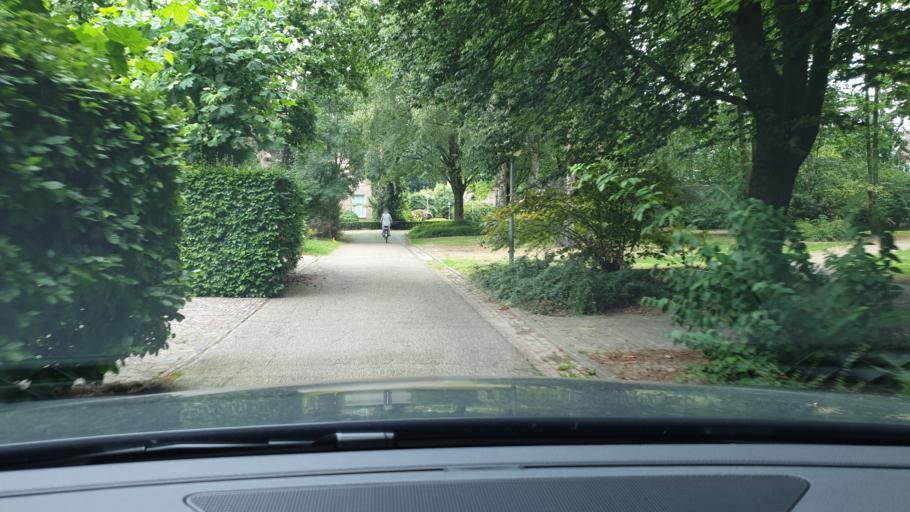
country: NL
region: North Brabant
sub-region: Gemeente Eindhoven
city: Meerhoven
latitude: 51.4281
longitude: 5.4156
